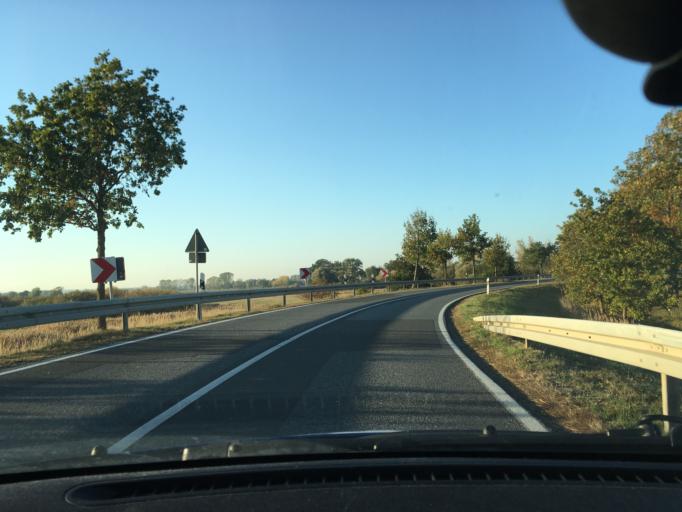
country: DE
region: Lower Saxony
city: Bleckede
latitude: 53.3369
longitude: 10.7981
